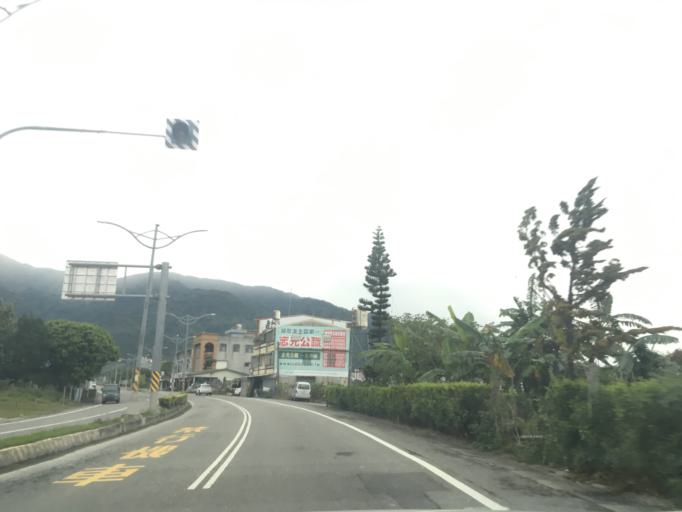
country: TW
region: Taiwan
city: Taitung City
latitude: 22.6943
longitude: 121.0458
